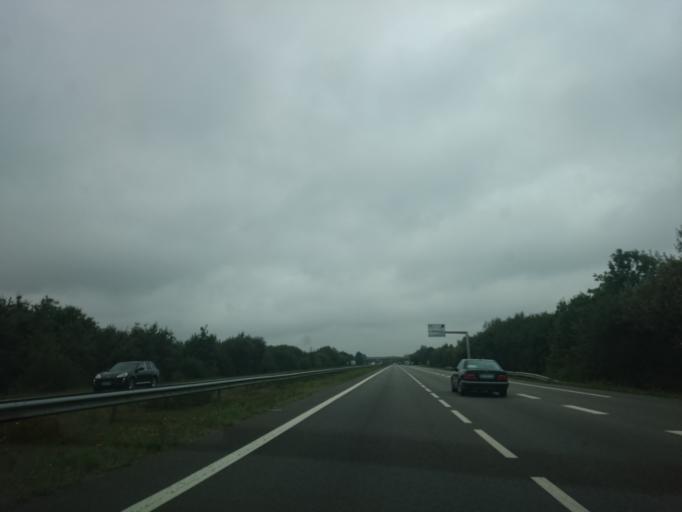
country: FR
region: Pays de la Loire
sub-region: Departement de la Loire-Atlantique
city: Bouguenais
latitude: 47.1687
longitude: -1.6486
